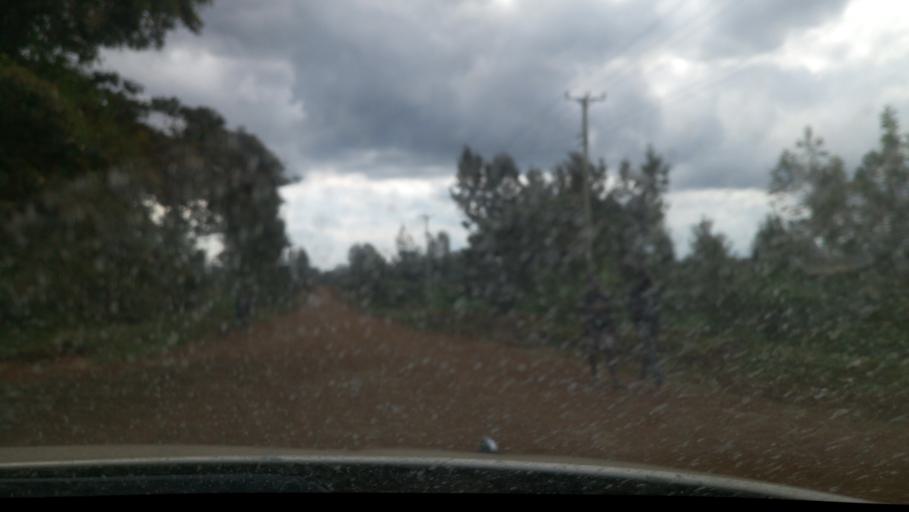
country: KE
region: Nairobi Area
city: Thika
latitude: -1.0031
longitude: 36.9180
